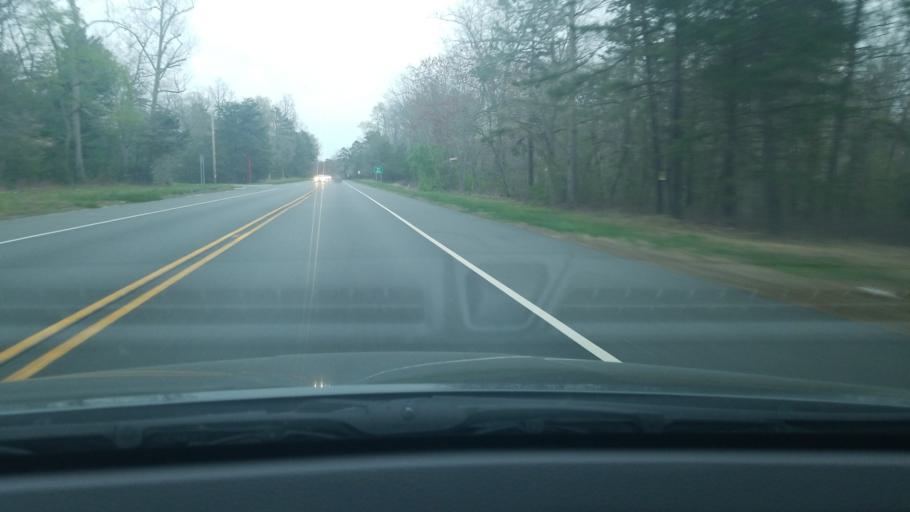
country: US
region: New Jersey
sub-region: Burlington County
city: Presidential Lakes Estates
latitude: 39.8916
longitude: -74.6256
